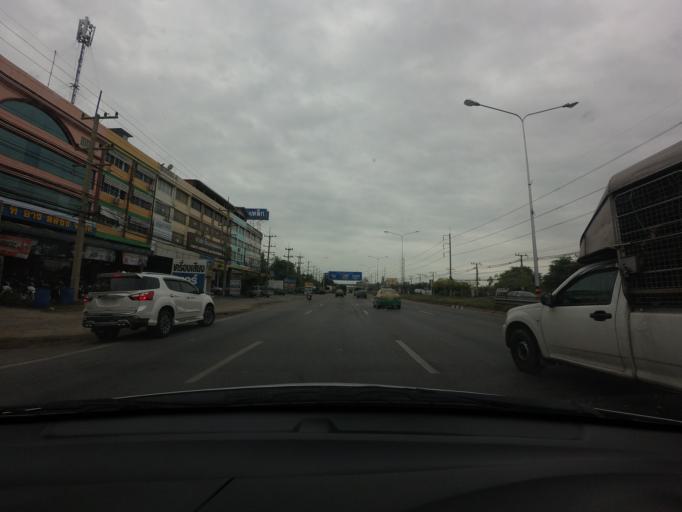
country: TH
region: Nakhon Pathom
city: Sam Phran
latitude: 13.7263
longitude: 100.2521
